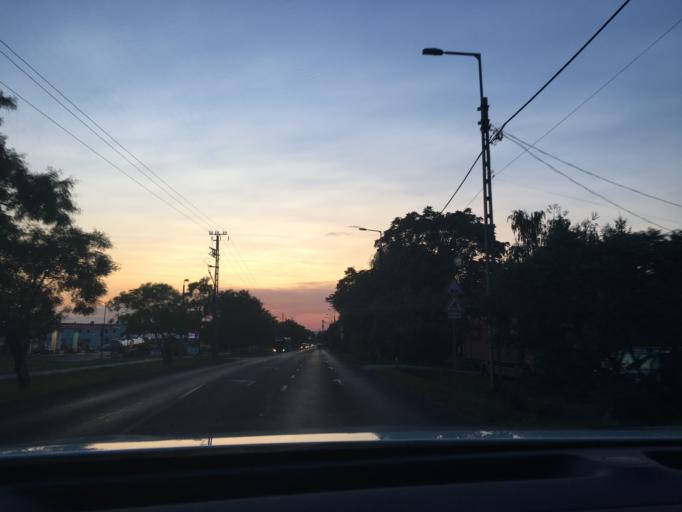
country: HU
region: Budapest
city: Budapest XVII. keruelet
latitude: 47.4732
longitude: 19.2754
